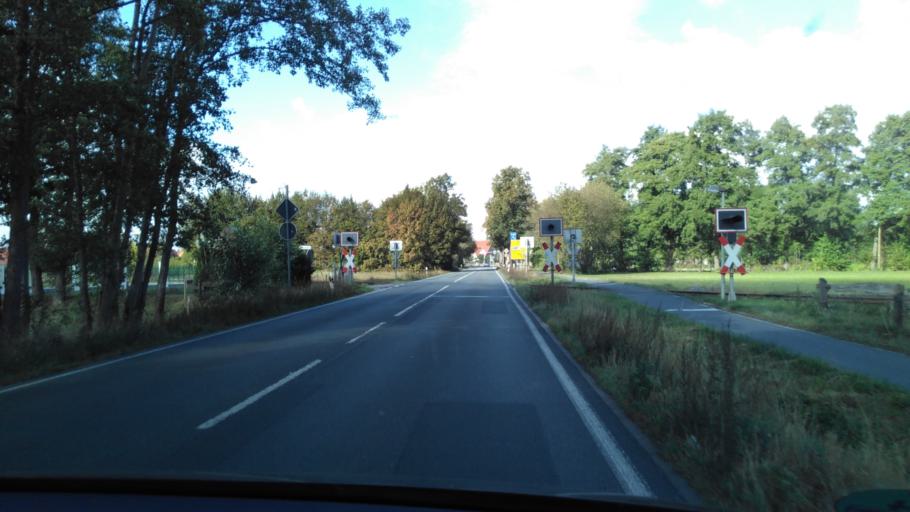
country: DE
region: North Rhine-Westphalia
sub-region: Regierungsbezirk Detmold
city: Verl
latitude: 51.8793
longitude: 8.5246
